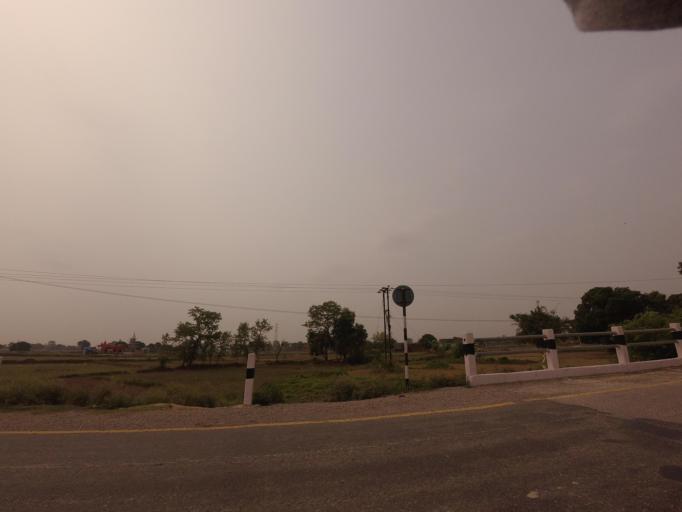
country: IN
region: Uttar Pradesh
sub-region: Maharajganj
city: Nautanwa
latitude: 27.5004
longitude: 83.3375
